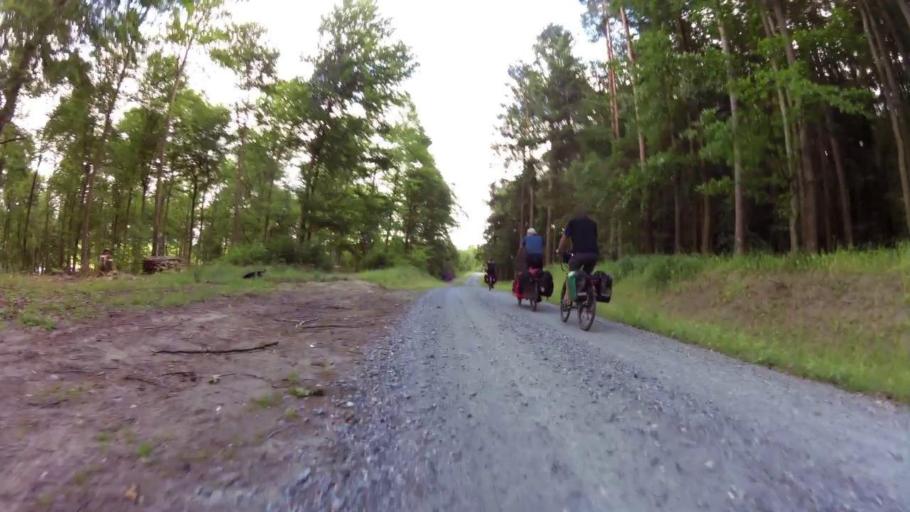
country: PL
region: West Pomeranian Voivodeship
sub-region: Powiat lobeski
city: Lobez
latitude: 53.6878
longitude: 15.5469
